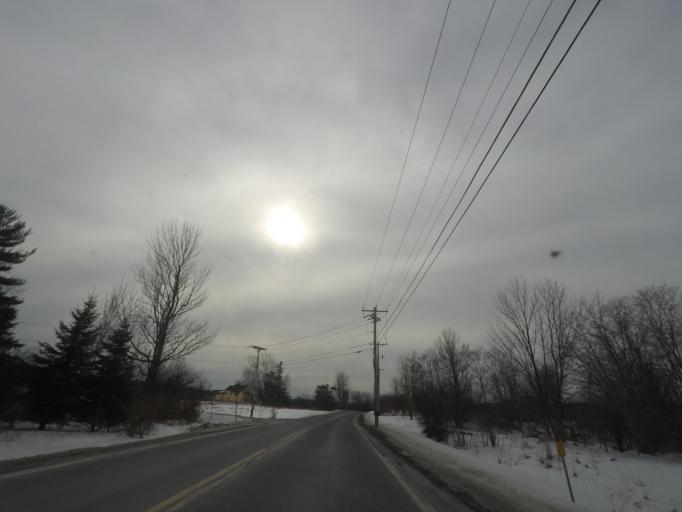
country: US
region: New York
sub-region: Albany County
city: Altamont
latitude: 42.6932
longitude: -74.0590
